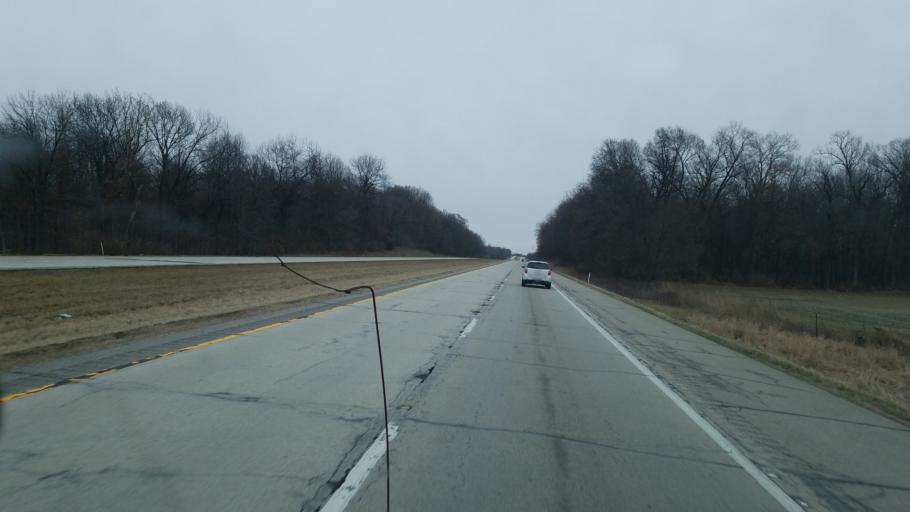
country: US
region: Indiana
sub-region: Starke County
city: Koontz Lake
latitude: 41.3644
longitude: -86.4184
